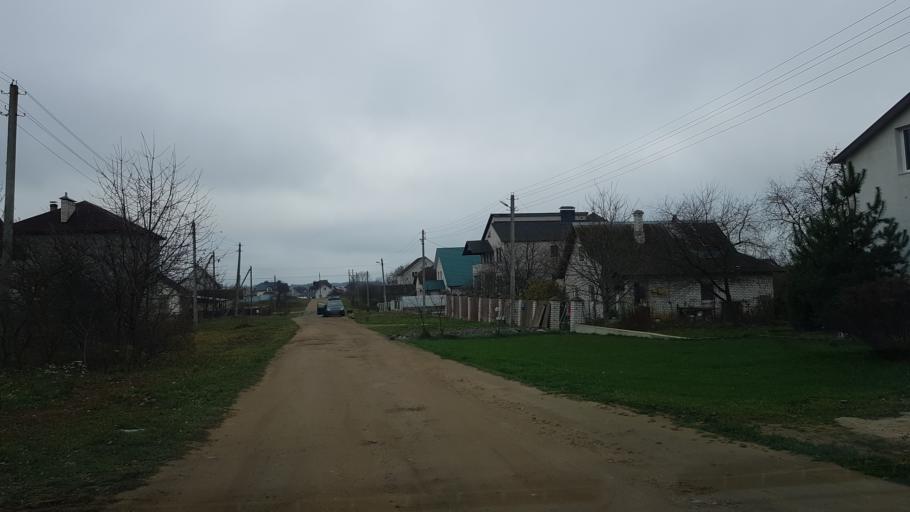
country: BY
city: Fanipol
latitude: 53.7327
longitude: 27.3149
